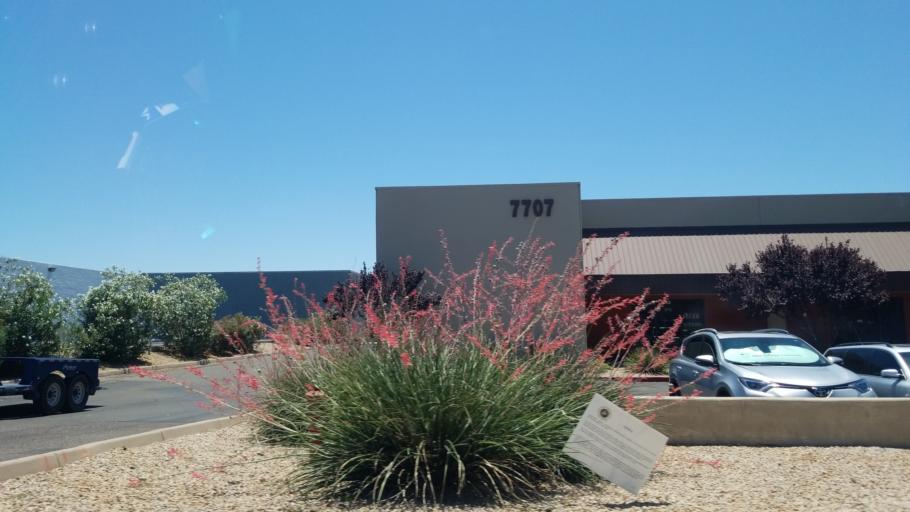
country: US
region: Arizona
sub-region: Maricopa County
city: Paradise Valley
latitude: 33.6177
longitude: -111.9121
